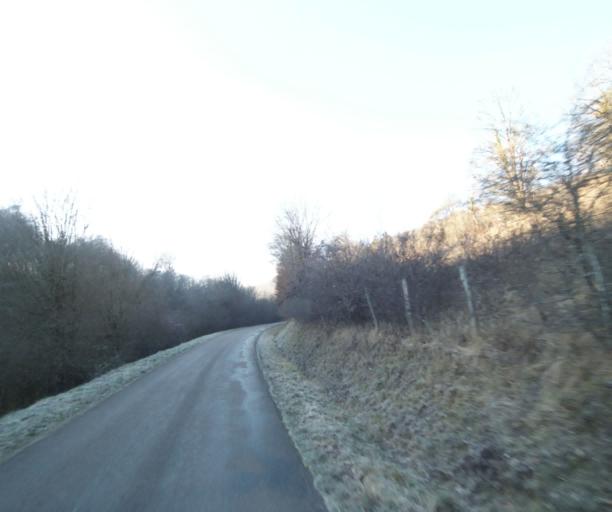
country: FR
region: Champagne-Ardenne
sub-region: Departement de la Haute-Marne
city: Joinville
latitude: 48.4903
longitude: 5.2180
